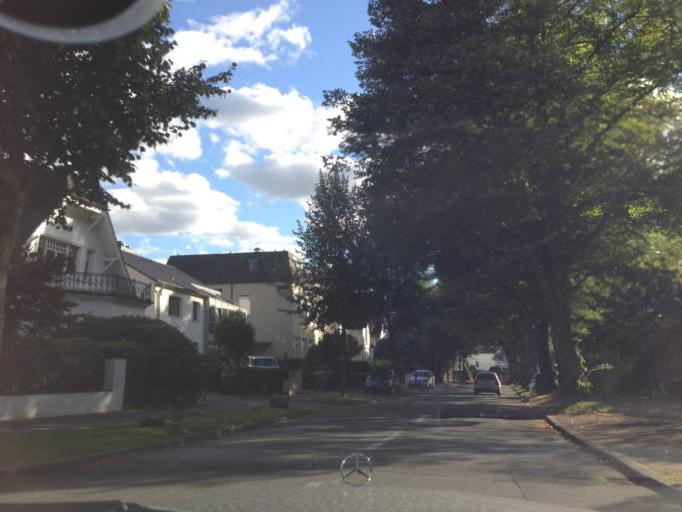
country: DE
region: Hamburg
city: Wandsbek
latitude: 53.5663
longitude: 10.0929
